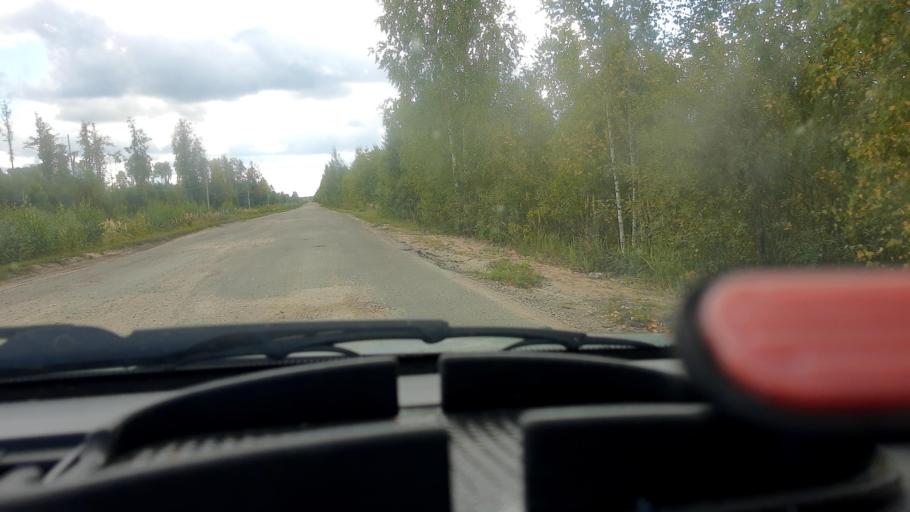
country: RU
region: Mariy-El
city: Kilemary
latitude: 56.8976
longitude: 46.7468
